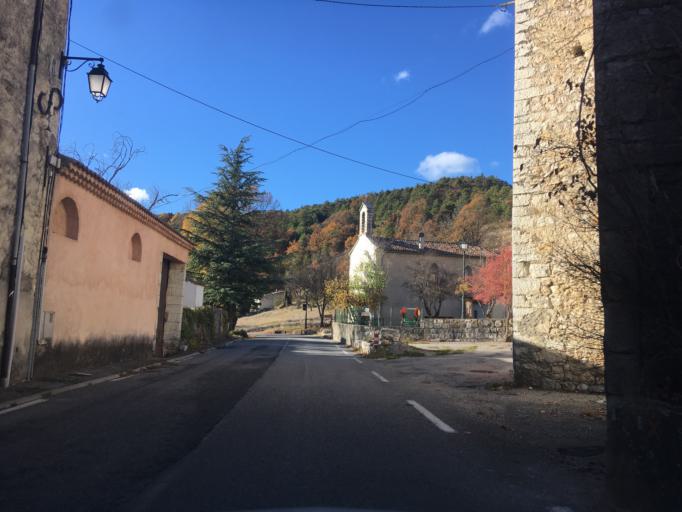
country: FR
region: Provence-Alpes-Cote d'Azur
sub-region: Departement des Alpes-de-Haute-Provence
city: Castellane
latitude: 43.7423
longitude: 6.4993
